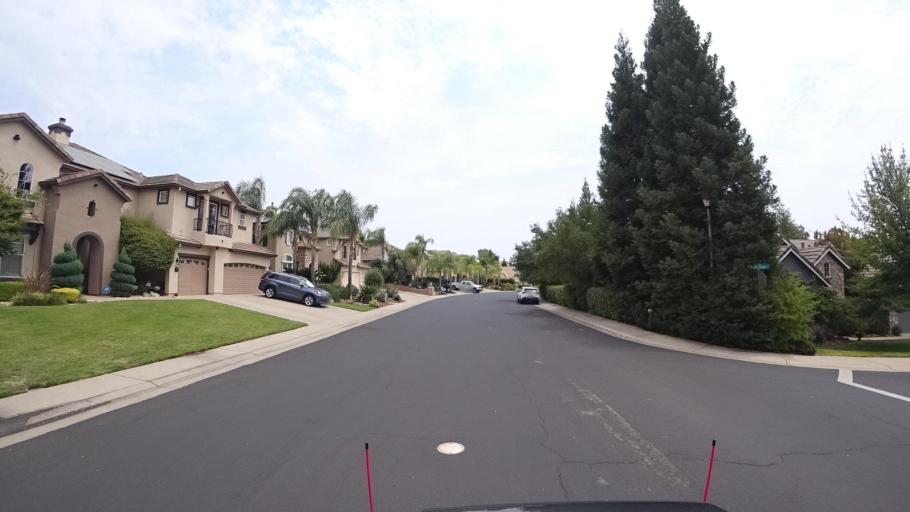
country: US
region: California
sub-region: Placer County
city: Rocklin
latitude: 38.7766
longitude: -121.2204
